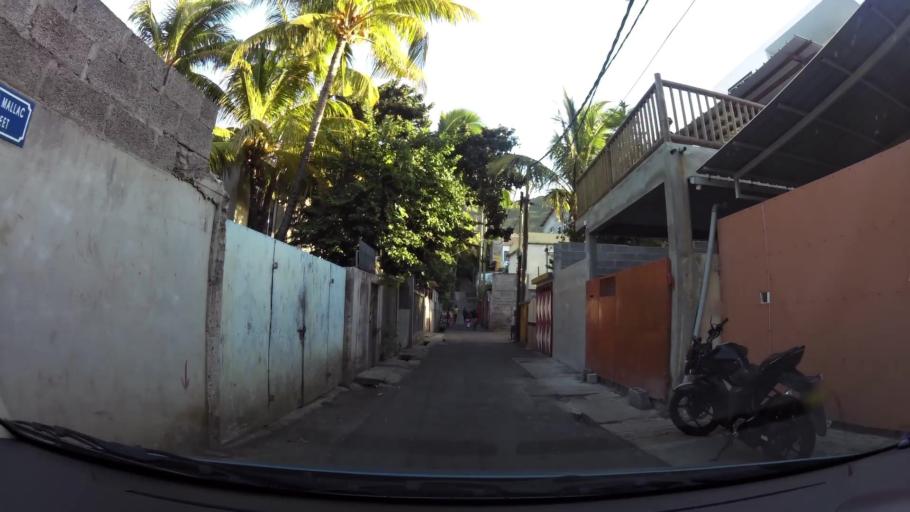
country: MU
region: Port Louis
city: Port Louis
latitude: -20.1781
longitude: 57.5127
